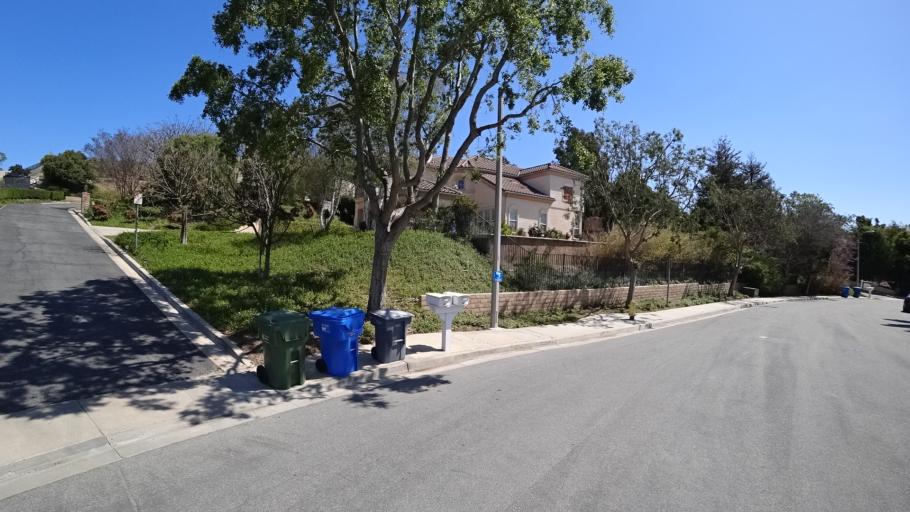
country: US
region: California
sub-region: Ventura County
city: Moorpark
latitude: 34.2322
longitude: -118.8856
